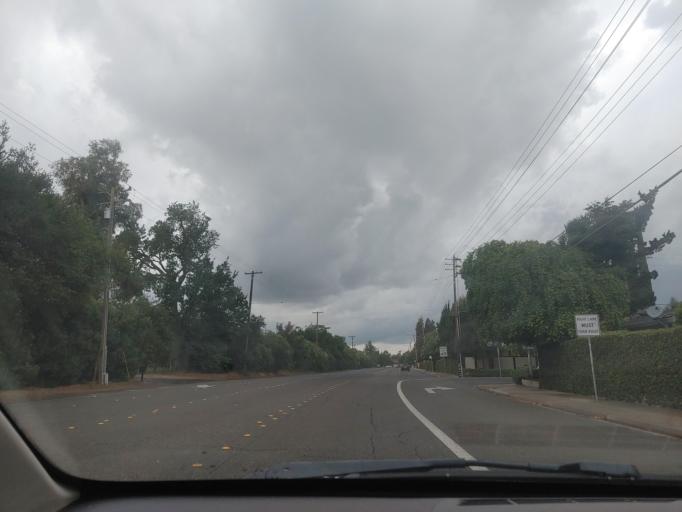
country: US
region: California
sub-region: Stanislaus County
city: Empire
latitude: 37.6526
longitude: -120.9477
